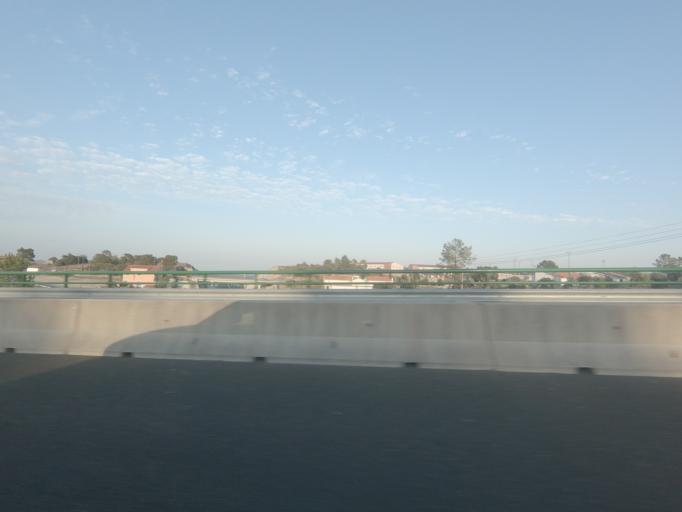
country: PT
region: Leiria
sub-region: Leiria
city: Santa Catarina da Serra
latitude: 39.6695
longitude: -8.6864
